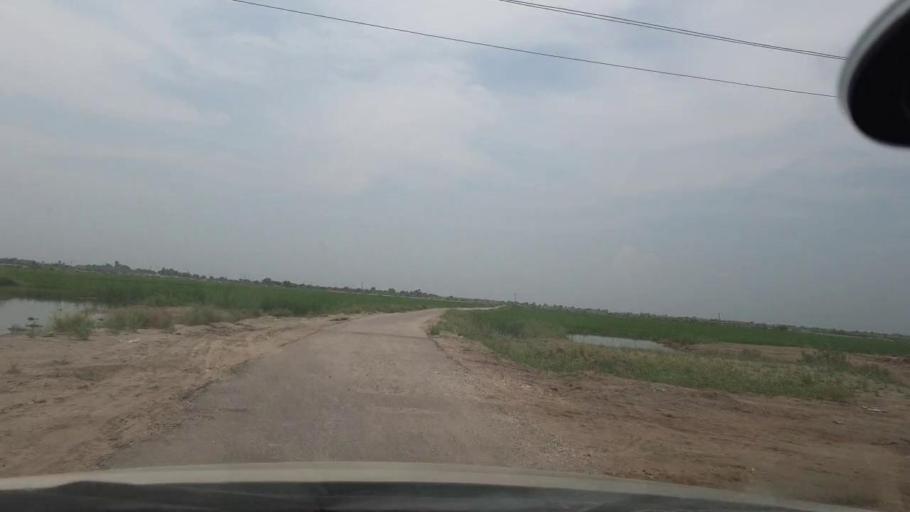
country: PK
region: Sindh
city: Jacobabad
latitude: 28.1410
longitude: 68.3475
